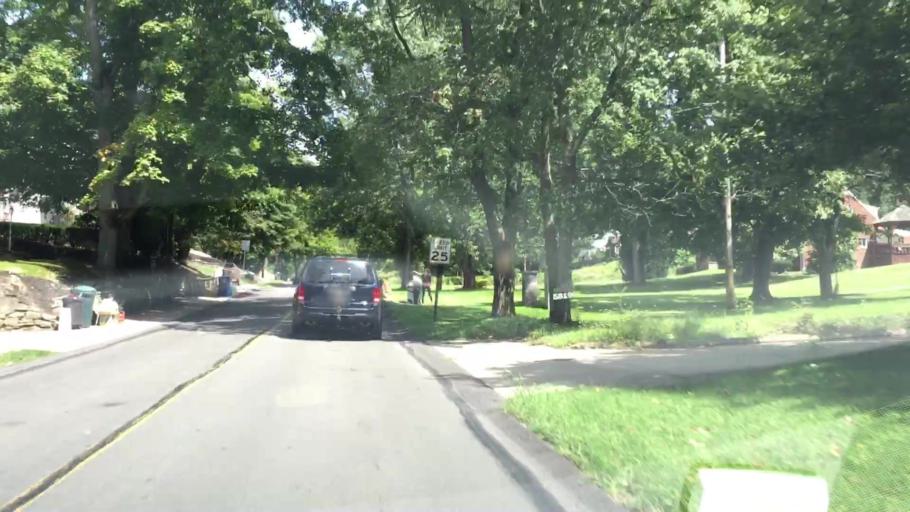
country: US
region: Pennsylvania
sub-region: Allegheny County
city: Bethel Park
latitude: 40.3094
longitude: -80.0301
